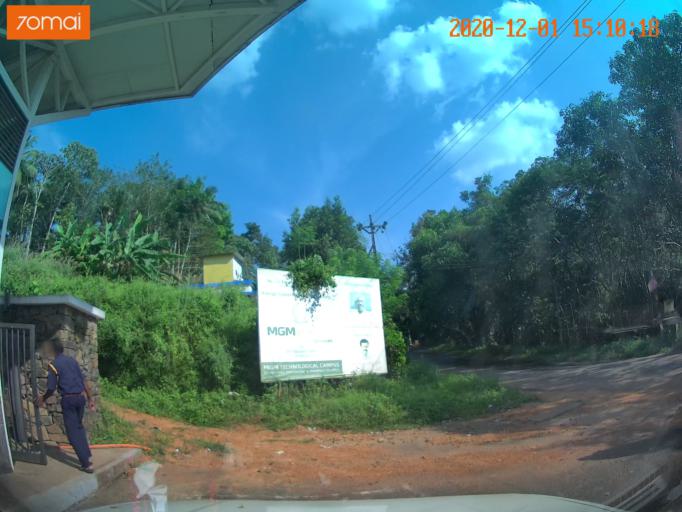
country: IN
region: Kerala
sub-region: Ernakulam
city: Ramamangalam
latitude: 9.9341
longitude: 76.5275
